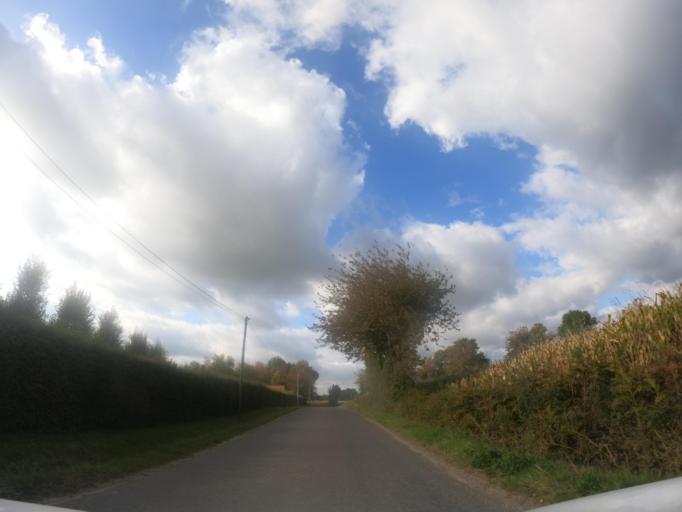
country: FR
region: Poitou-Charentes
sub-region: Departement des Deux-Sevres
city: La Foret-sur-Sevre
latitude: 46.7903
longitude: -0.6114
